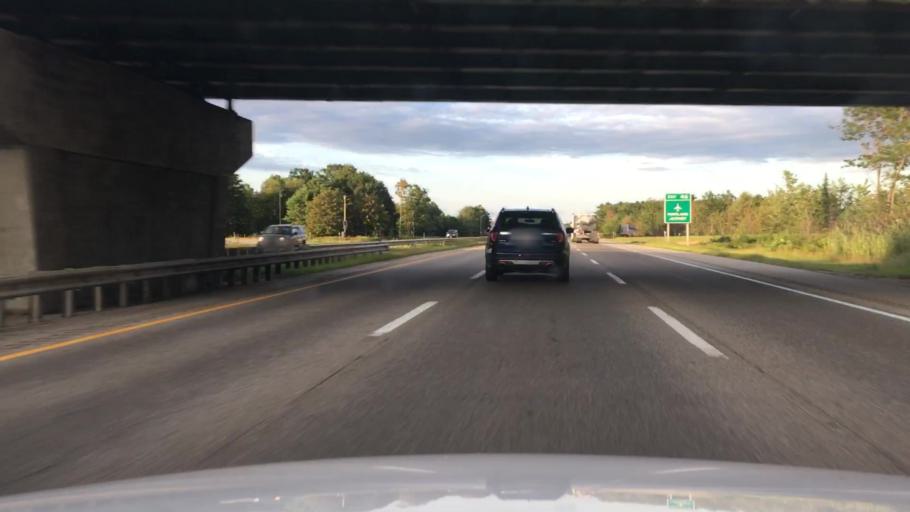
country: US
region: Maine
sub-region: Cumberland County
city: West Scarborough
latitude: 43.6050
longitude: -70.3722
